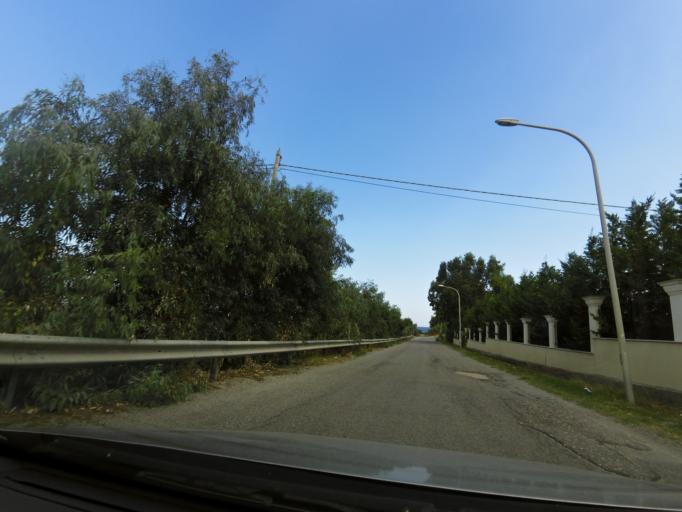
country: IT
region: Calabria
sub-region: Provincia di Reggio Calabria
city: Monasterace Marina
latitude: 38.4205
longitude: 16.5595
